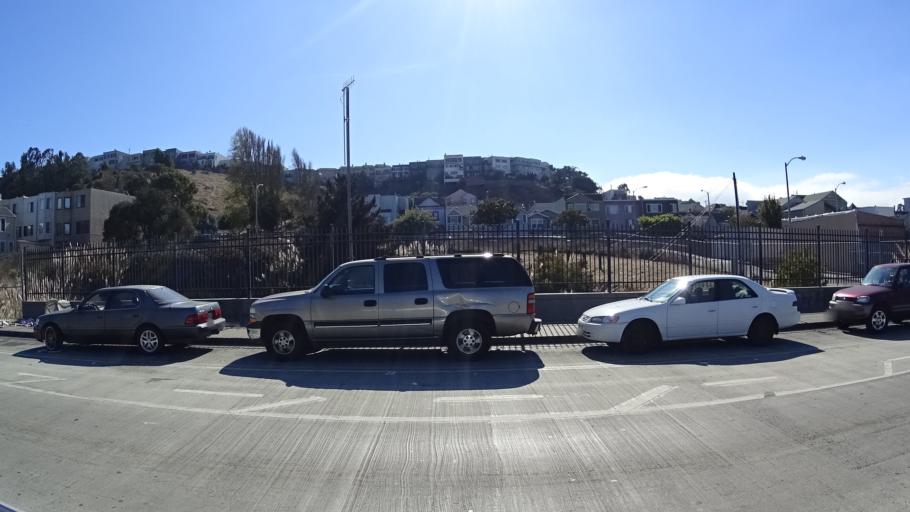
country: US
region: California
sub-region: San Francisco County
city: San Francisco
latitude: 37.7372
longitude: -122.3948
